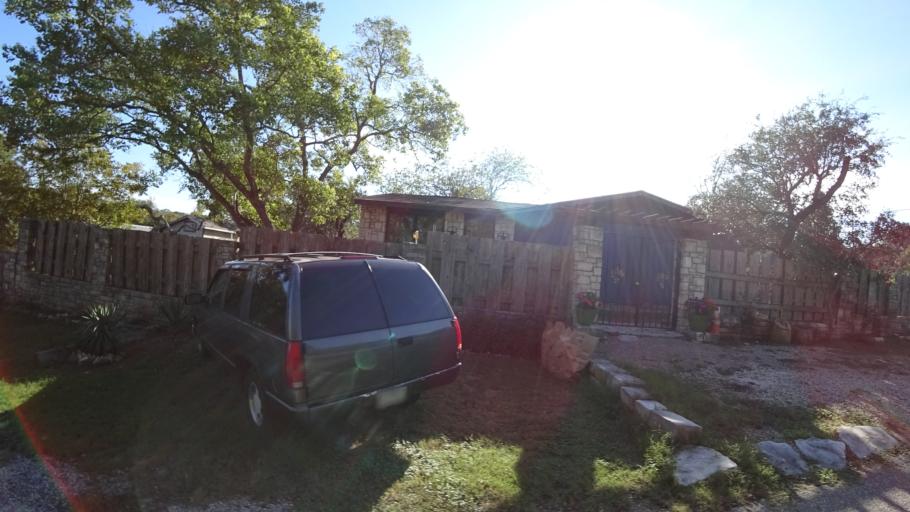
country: US
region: Texas
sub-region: Travis County
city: Barton Creek
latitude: 30.2426
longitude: -97.9173
